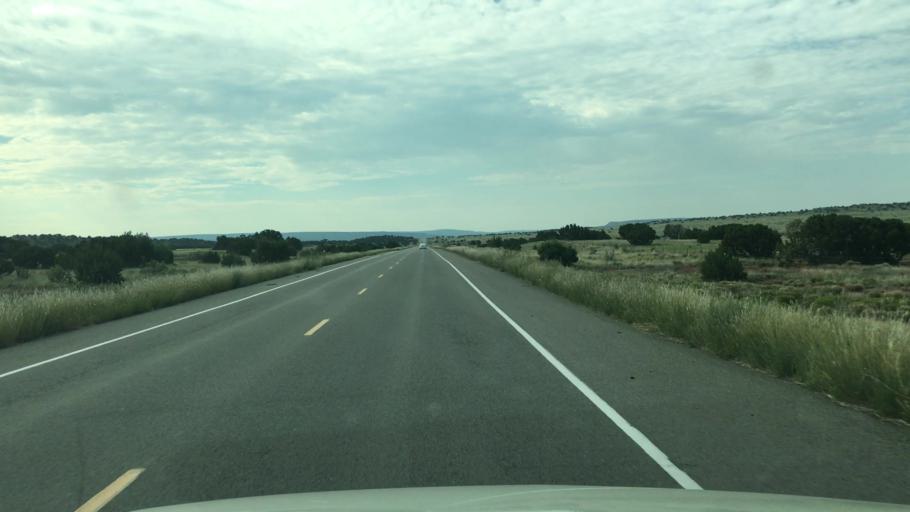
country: US
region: New Mexico
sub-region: Santa Fe County
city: Eldorado at Santa Fe
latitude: 35.4465
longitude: -105.8882
